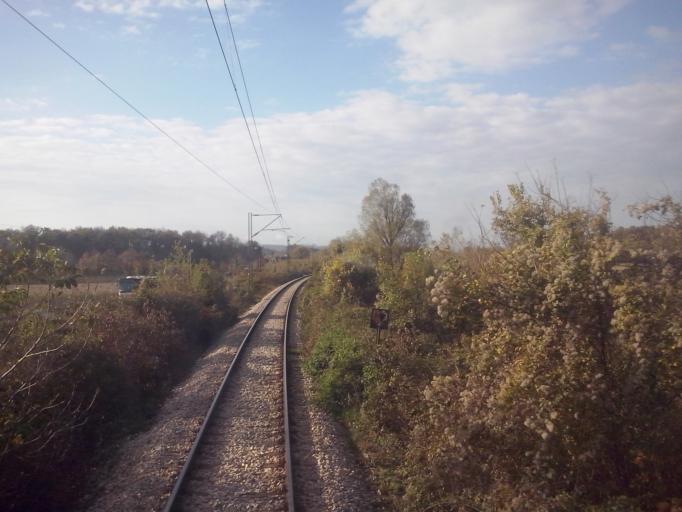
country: RS
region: Central Serbia
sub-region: Belgrade
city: Lazarevac
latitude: 44.4152
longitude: 20.2739
